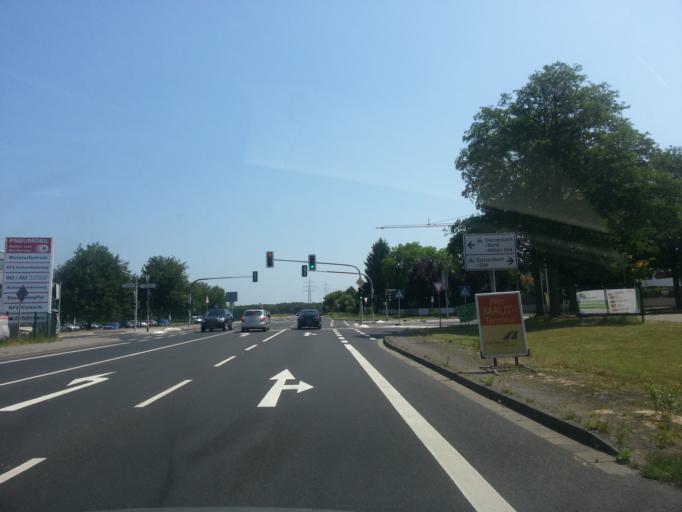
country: DE
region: Hesse
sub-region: Regierungsbezirk Darmstadt
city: Dietzenbach
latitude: 50.0028
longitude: 8.7935
